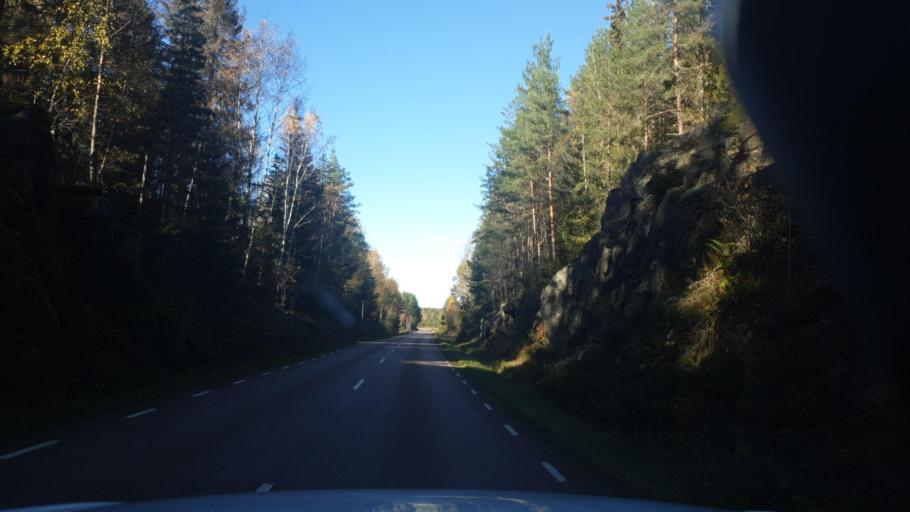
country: SE
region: Vaermland
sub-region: Grums Kommun
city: Slottsbron
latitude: 59.4056
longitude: 13.0071
